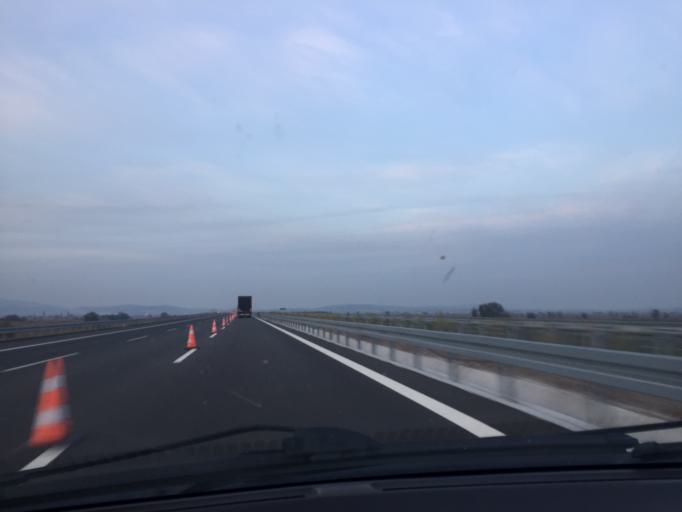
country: TR
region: Manisa
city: Halitpasa
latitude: 38.7262
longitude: 27.6538
